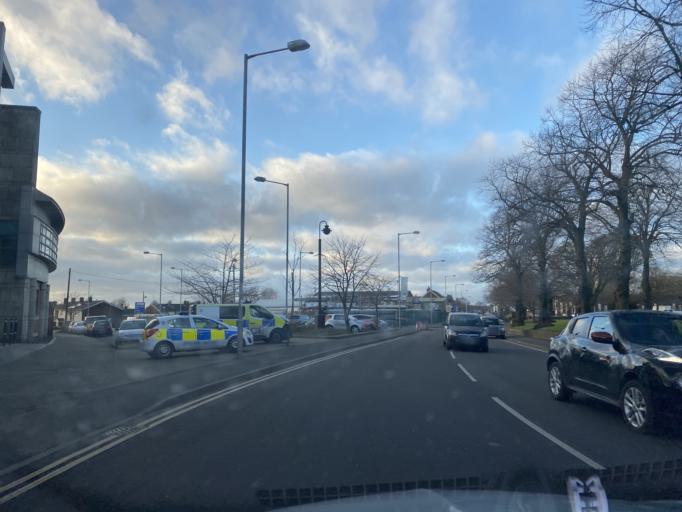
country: GB
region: England
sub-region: Walsall
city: Bloxwich
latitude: 52.6146
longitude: -2.0052
